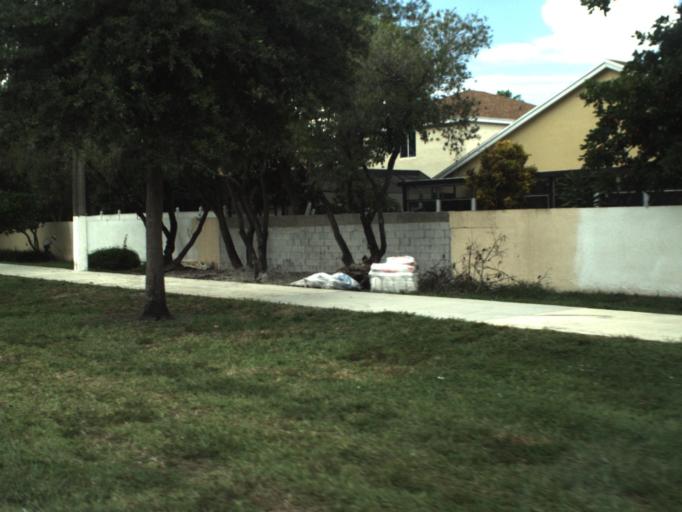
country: US
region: Florida
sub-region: Miami-Dade County
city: Lake Lucerne
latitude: 25.9810
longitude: -80.2689
